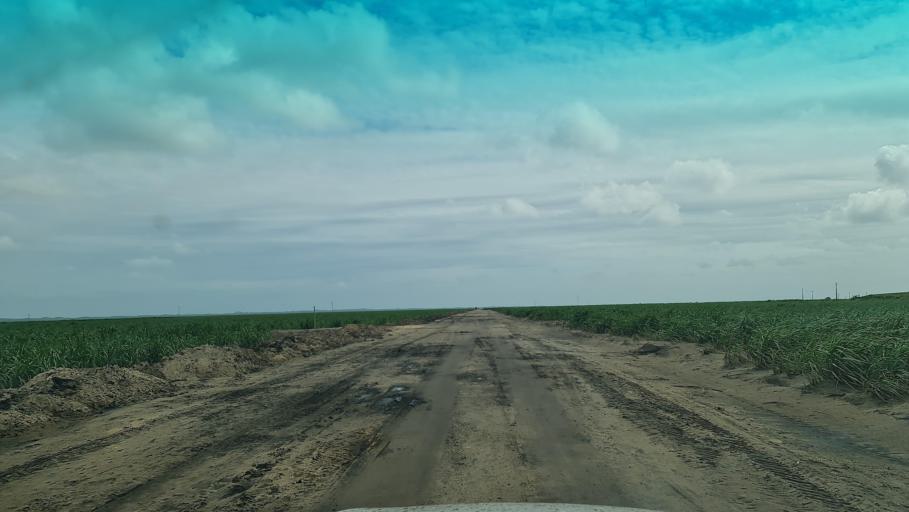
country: MZ
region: Maputo
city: Manhica
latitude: -25.4687
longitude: 32.8175
